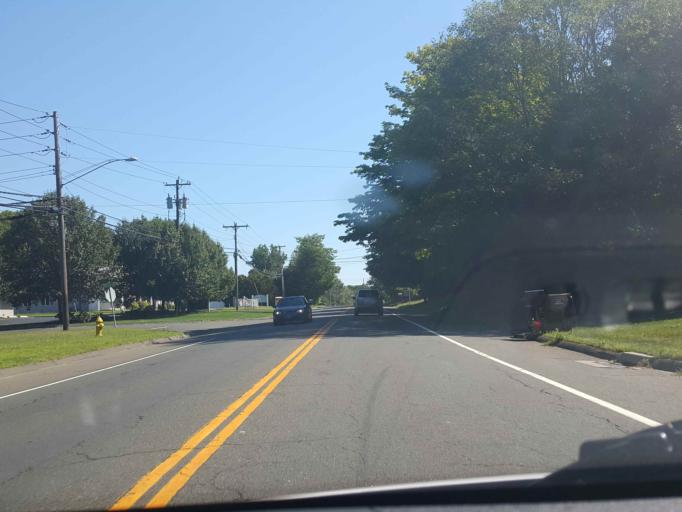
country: US
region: Connecticut
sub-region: New Haven County
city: North Branford
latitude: 41.3395
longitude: -72.7517
